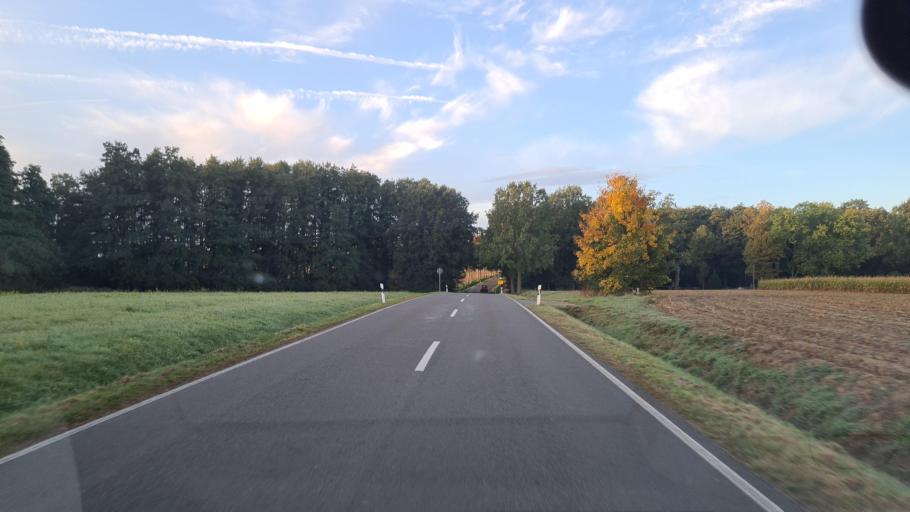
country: DE
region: Saxony
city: Machern
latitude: 51.3722
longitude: 12.6436
